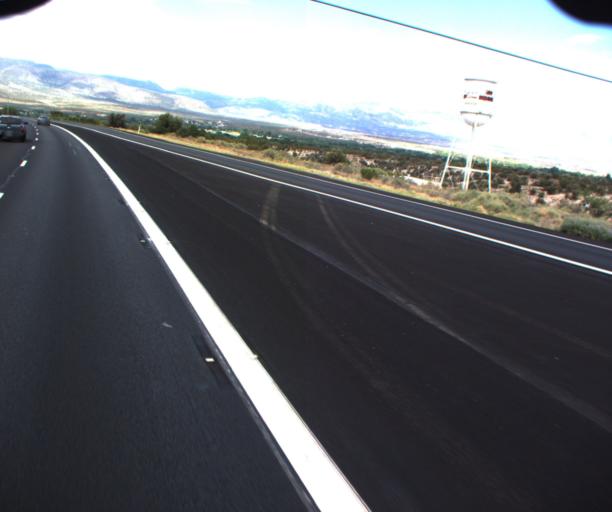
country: US
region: Arizona
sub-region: Yavapai County
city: Camp Verde
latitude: 34.6105
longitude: -111.8645
